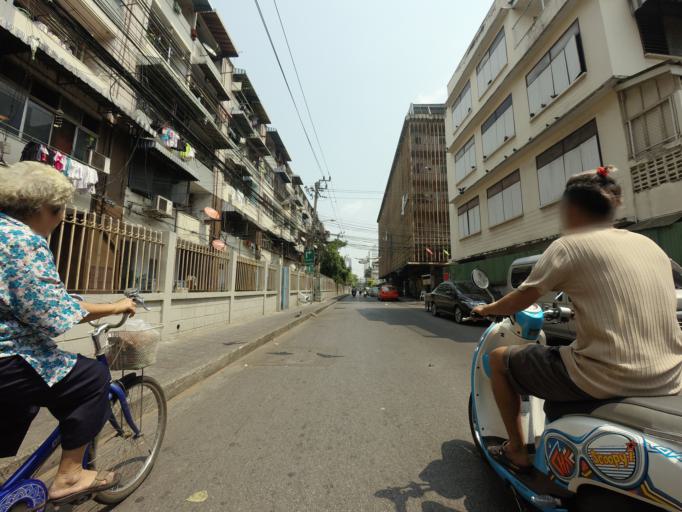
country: TH
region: Bangkok
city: Din Daeng
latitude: 13.7615
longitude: 100.5519
